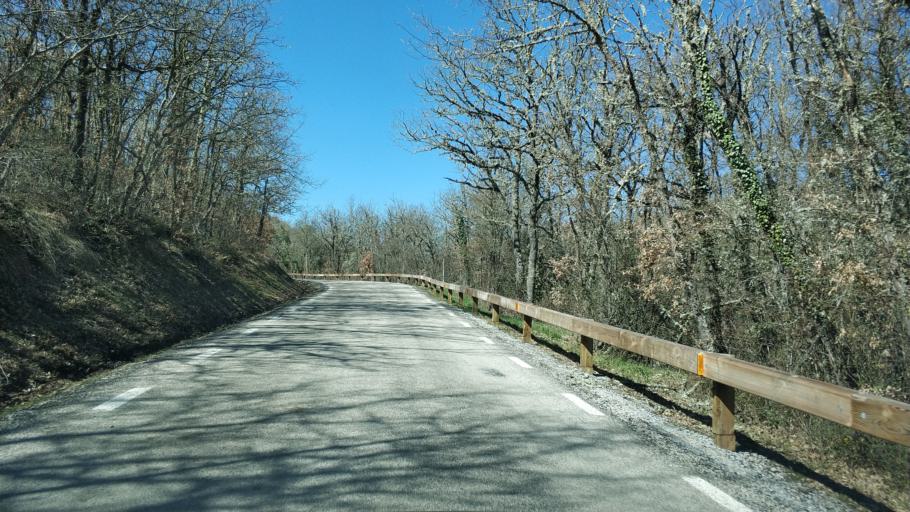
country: ES
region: Castille and Leon
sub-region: Provincia de Palencia
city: Berzosilla
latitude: 42.8694
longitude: -4.0655
